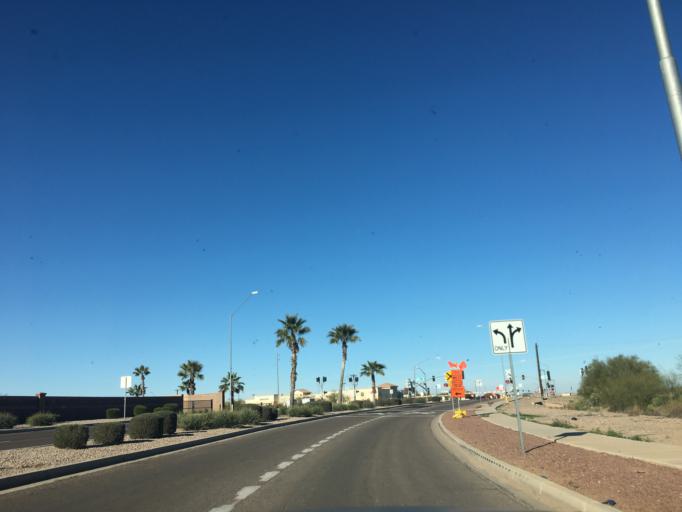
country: US
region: Arizona
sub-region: Pinal County
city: Maricopa
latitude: 33.0342
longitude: -112.0141
